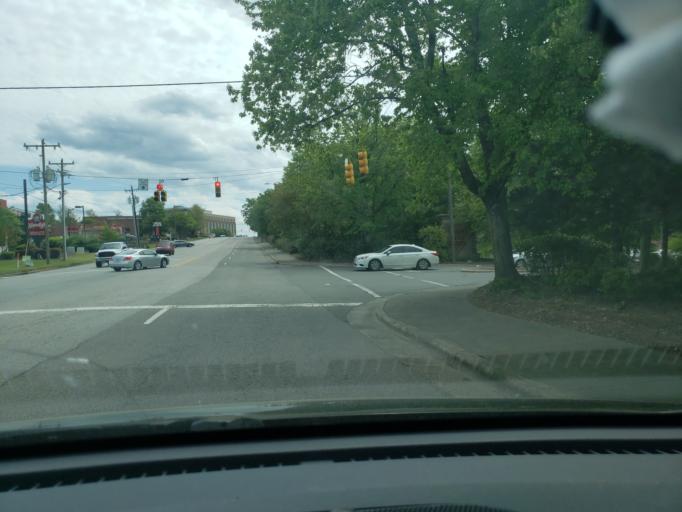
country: US
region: North Carolina
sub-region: Durham County
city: Durham
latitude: 35.9685
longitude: -78.9551
